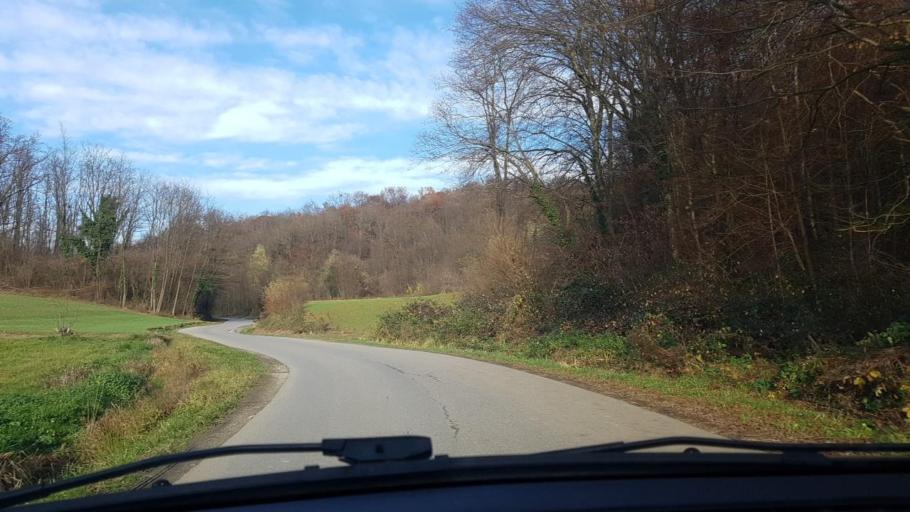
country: HR
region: Krapinsko-Zagorska
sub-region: Grad Krapina
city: Krapina
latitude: 46.1279
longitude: 15.8716
